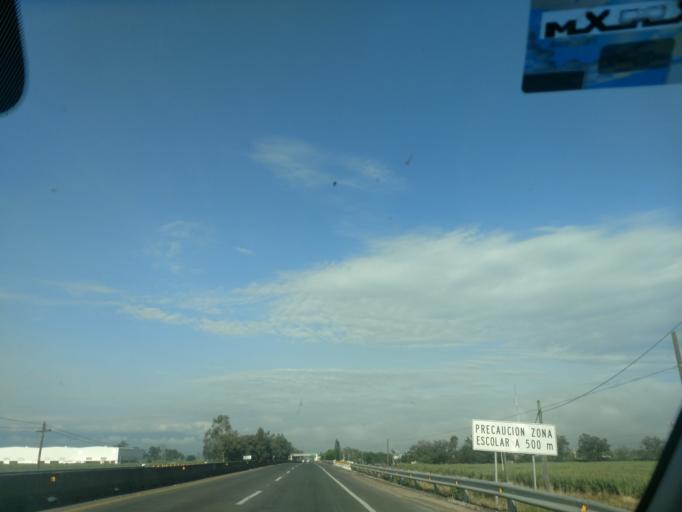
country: MX
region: Jalisco
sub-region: Ameca
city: Los Pocitos
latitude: 20.5349
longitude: -103.9604
